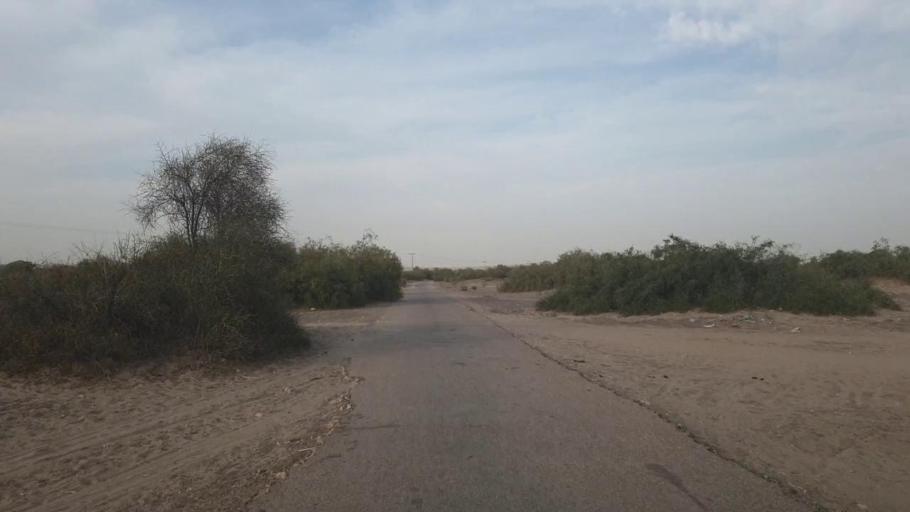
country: PK
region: Sindh
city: Nabisar
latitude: 25.1027
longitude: 69.6744
